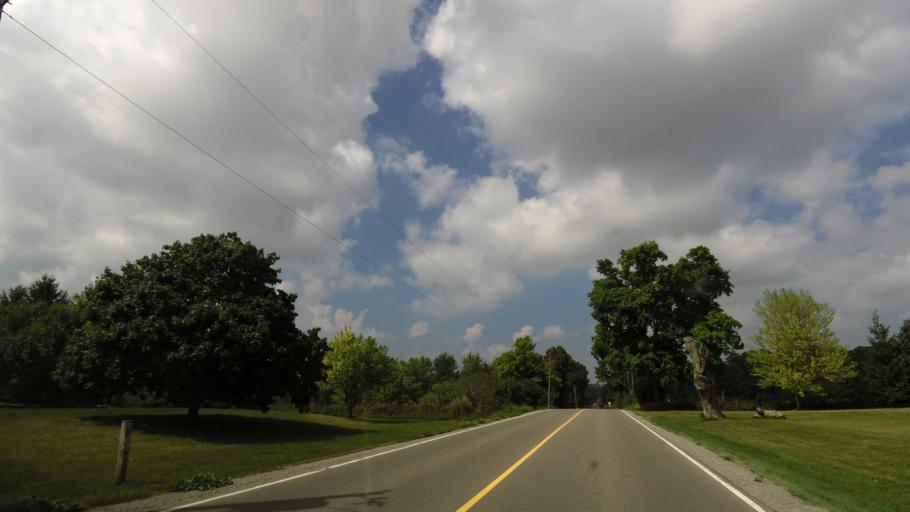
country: CA
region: Ontario
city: Oshawa
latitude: 43.9884
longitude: -78.8709
